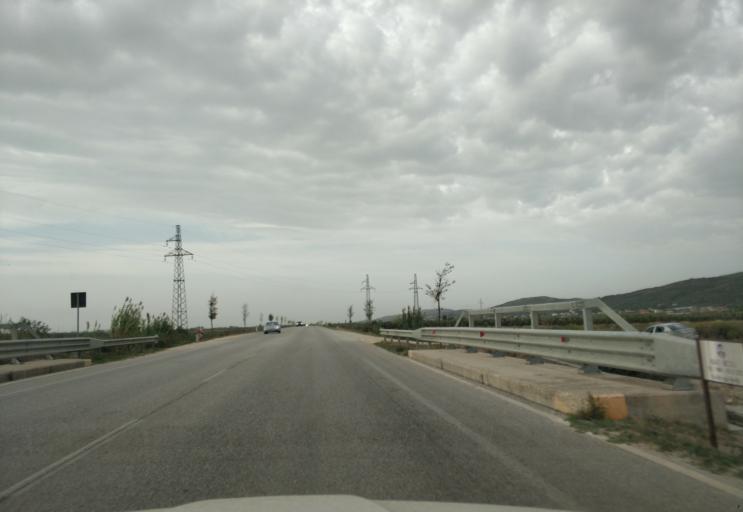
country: AL
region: Fier
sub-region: Rrethi i Fierit
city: Frakulla e Madhe
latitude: 40.6395
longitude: 19.5023
